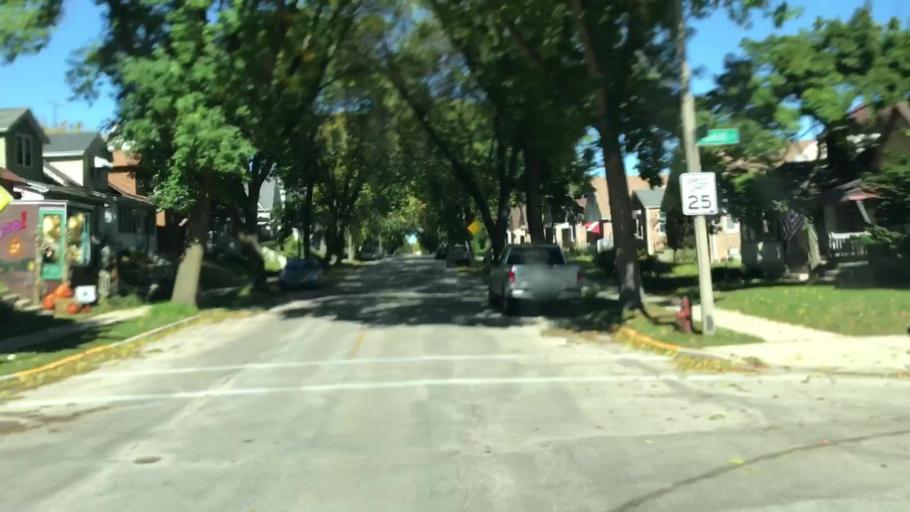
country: US
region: Wisconsin
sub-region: Milwaukee County
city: Saint Francis
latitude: 42.9910
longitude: -87.8943
